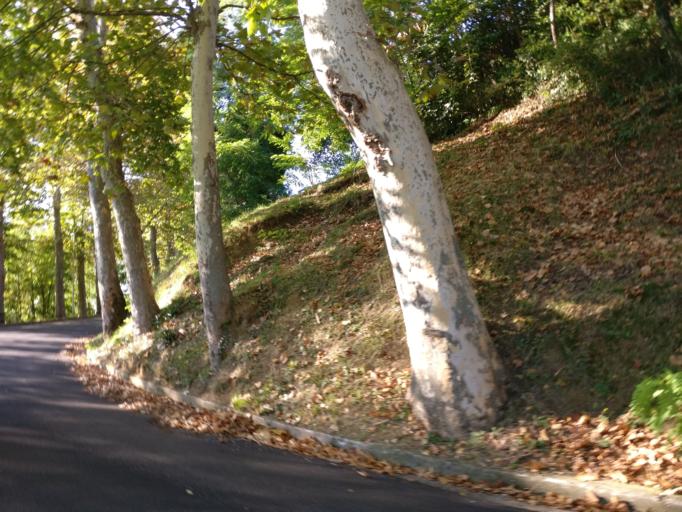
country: IT
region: The Marches
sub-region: Provincia di Ascoli Piceno
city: Montedinove
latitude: 42.9729
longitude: 13.5903
